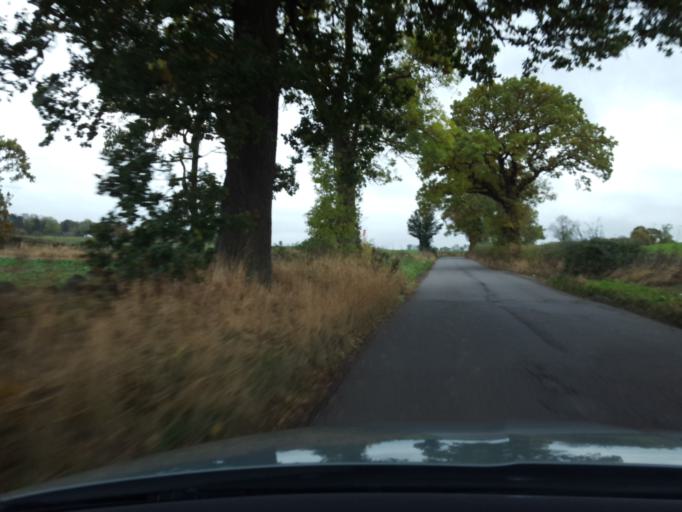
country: GB
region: Scotland
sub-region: Edinburgh
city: Newbridge
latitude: 55.9139
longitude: -3.4169
